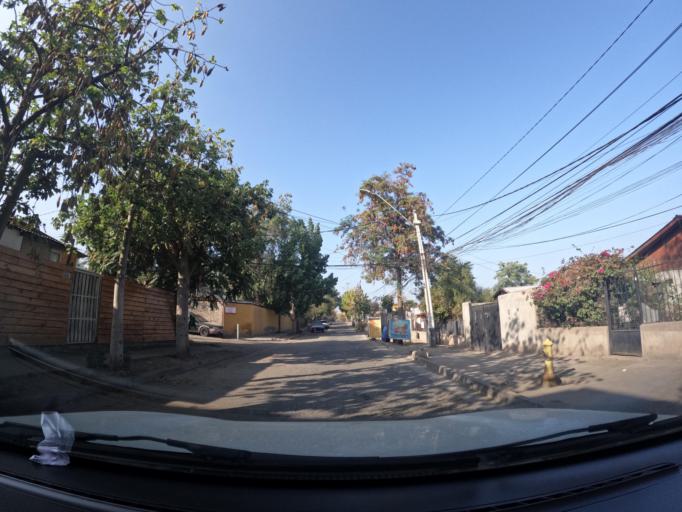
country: CL
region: Santiago Metropolitan
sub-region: Provincia de Santiago
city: Villa Presidente Frei, Nunoa, Santiago, Chile
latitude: -33.4707
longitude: -70.5343
